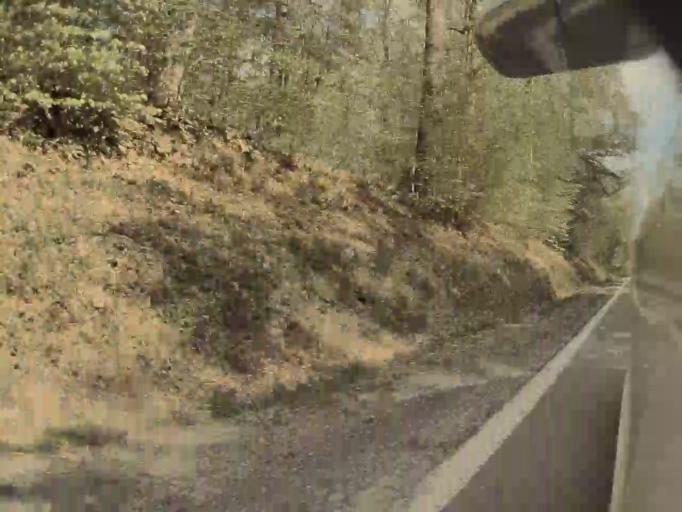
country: BE
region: Wallonia
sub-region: Province du Luxembourg
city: Tellin
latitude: 50.0441
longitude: 5.2090
